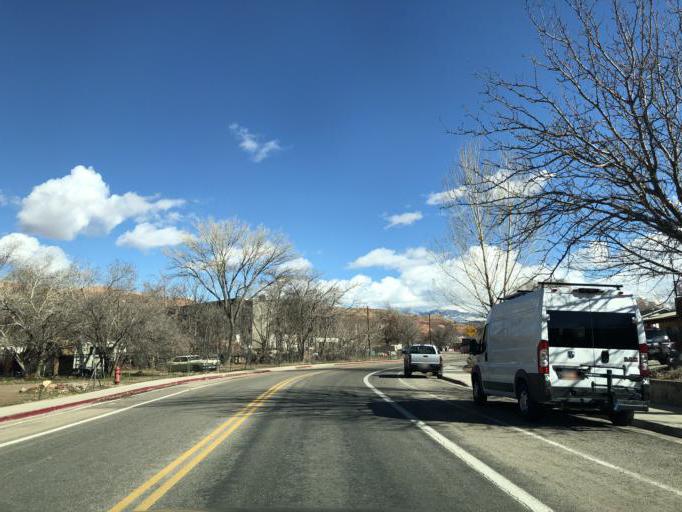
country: US
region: Utah
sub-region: Grand County
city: Moab
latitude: 38.5744
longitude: -109.5559
